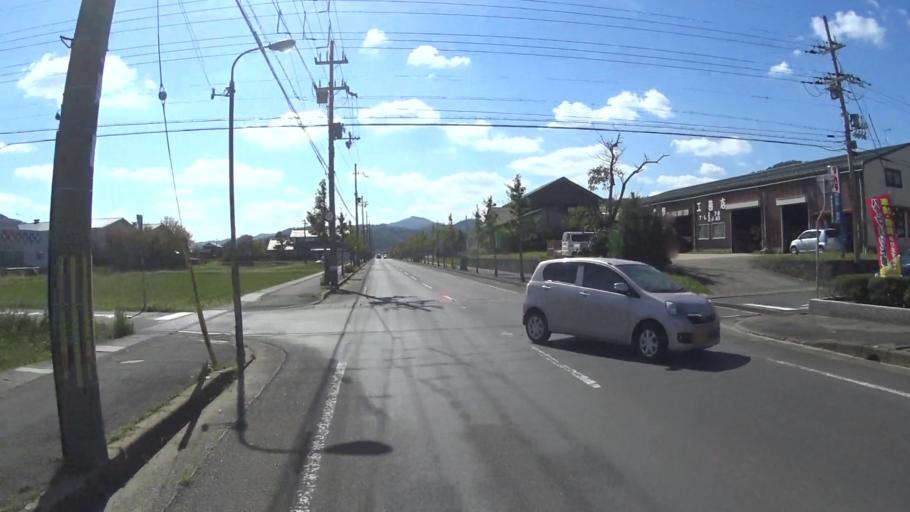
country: JP
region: Kyoto
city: Miyazu
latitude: 35.6772
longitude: 135.0249
